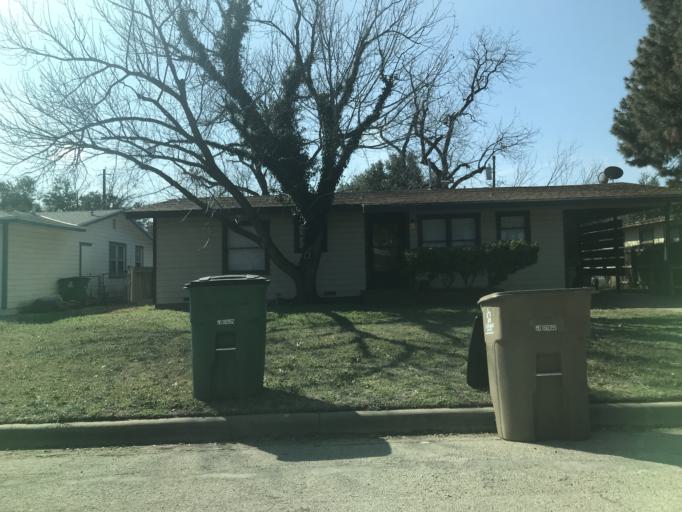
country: US
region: Texas
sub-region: Tom Green County
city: San Angelo
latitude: 31.4281
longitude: -100.4634
